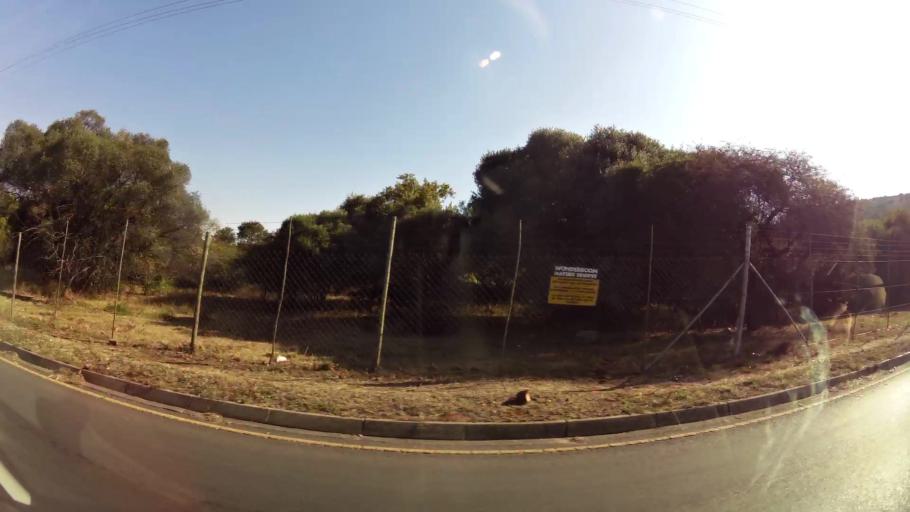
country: ZA
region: Gauteng
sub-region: City of Tshwane Metropolitan Municipality
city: Pretoria
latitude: -25.6959
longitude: 28.1988
